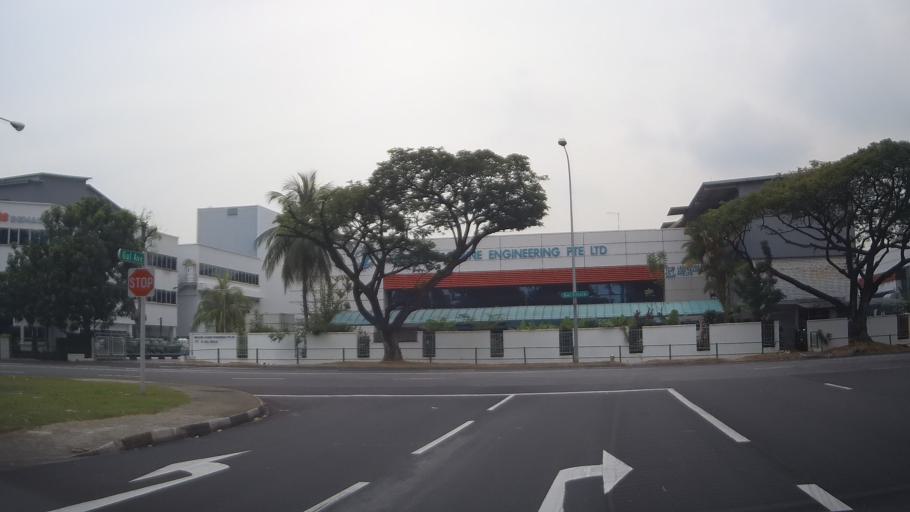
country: MY
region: Johor
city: Johor Bahru
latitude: 1.3137
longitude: 103.6651
